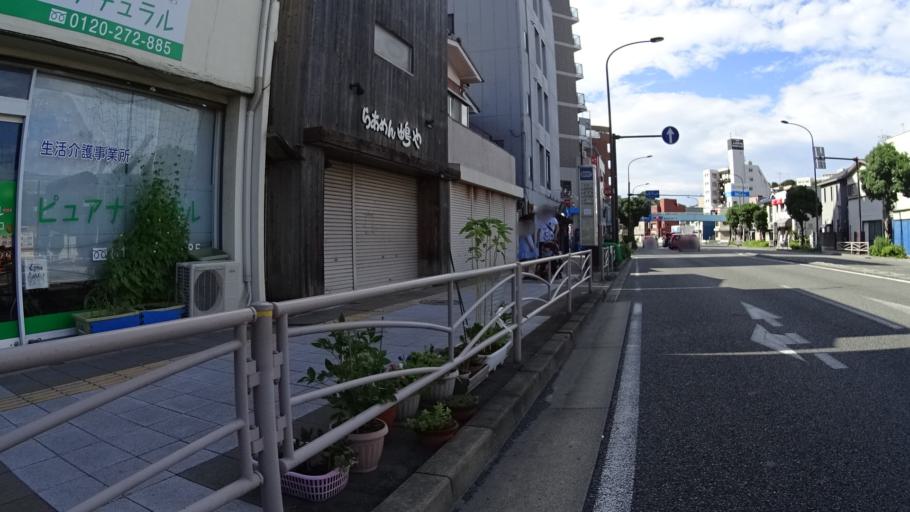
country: JP
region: Kanagawa
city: Yokosuka
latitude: 35.2739
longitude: 139.6770
